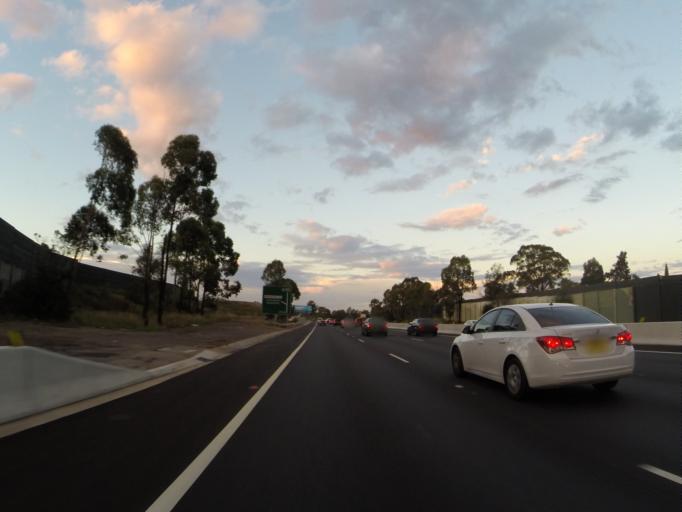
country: AU
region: New South Wales
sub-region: Campbelltown Municipality
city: Glenfield
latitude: -33.9408
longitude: 150.9023
